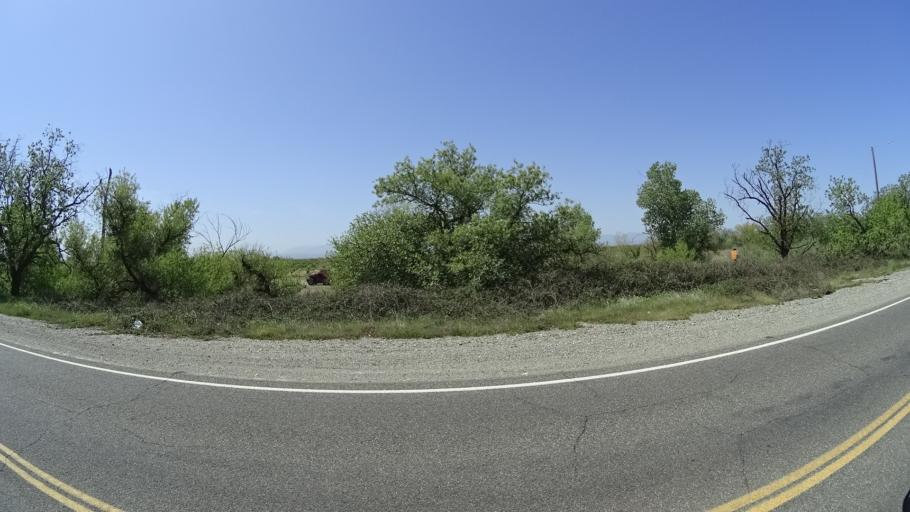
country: US
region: California
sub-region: Glenn County
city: Willows
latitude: 39.6267
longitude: -122.1971
